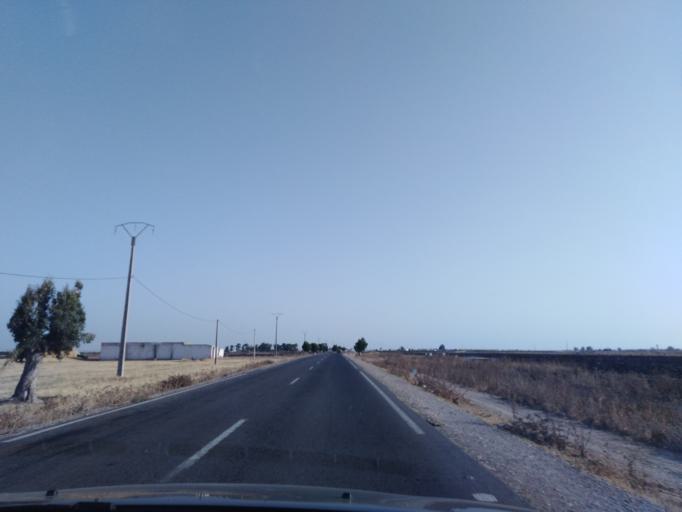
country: MA
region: Doukkala-Abda
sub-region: Safi
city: Youssoufia
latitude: 32.4793
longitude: -8.7698
